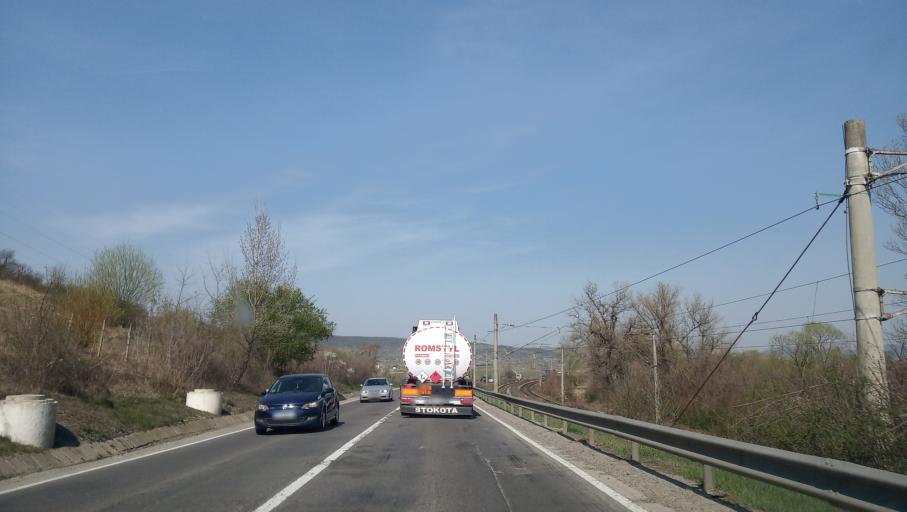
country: RO
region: Alba
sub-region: Comuna Radesti
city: Radesti
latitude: 46.2718
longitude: 23.6988
